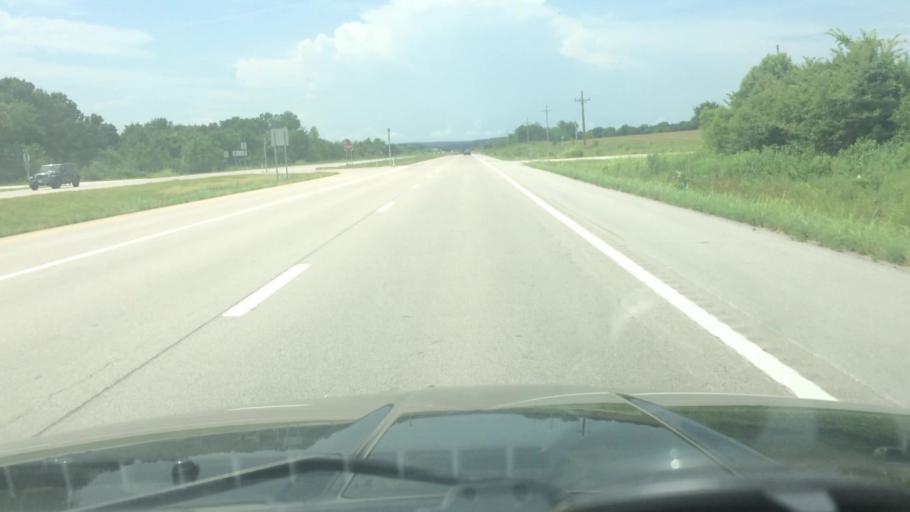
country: US
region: Missouri
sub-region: Polk County
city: Humansville
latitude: 37.8048
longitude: -93.5989
